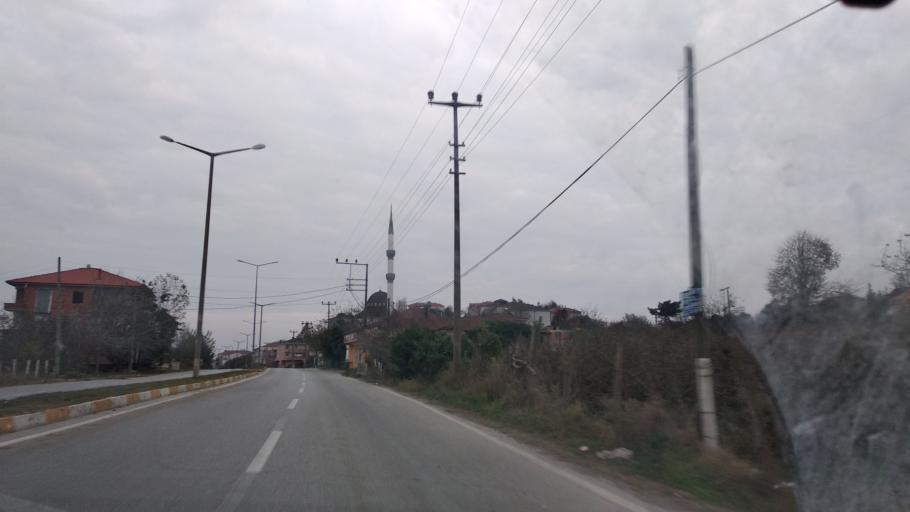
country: TR
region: Sakarya
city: Karasu
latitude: 41.0985
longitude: 30.6729
